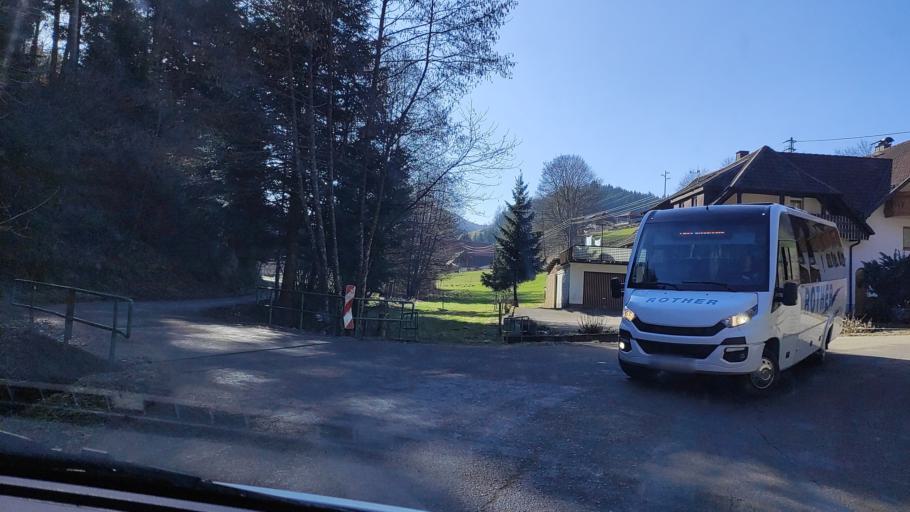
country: DE
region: Baden-Wuerttemberg
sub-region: Freiburg Region
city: Elzach
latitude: 48.1968
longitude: 8.0140
